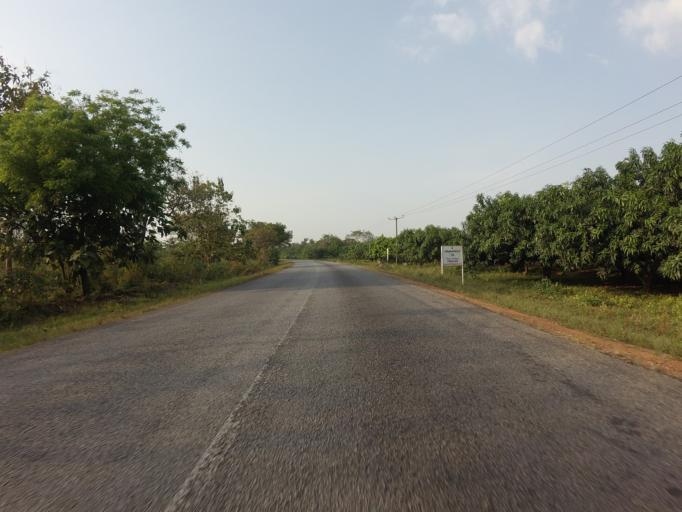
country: GH
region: Volta
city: Ho
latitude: 6.4017
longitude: 0.1780
